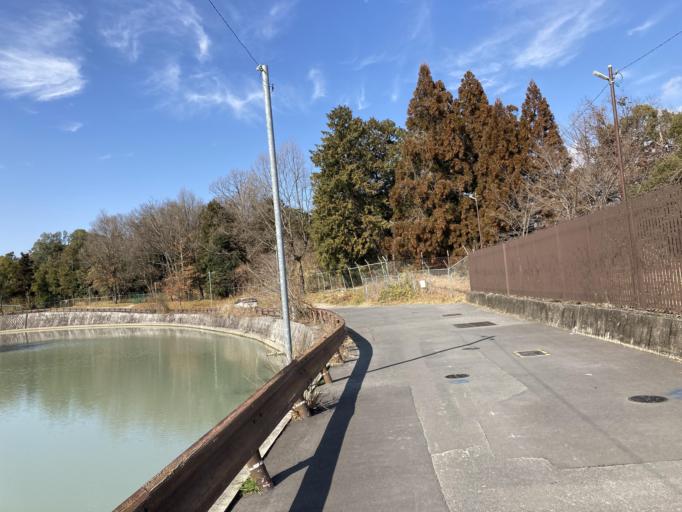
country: JP
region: Nara
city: Nara-shi
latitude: 34.6984
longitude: 135.8058
